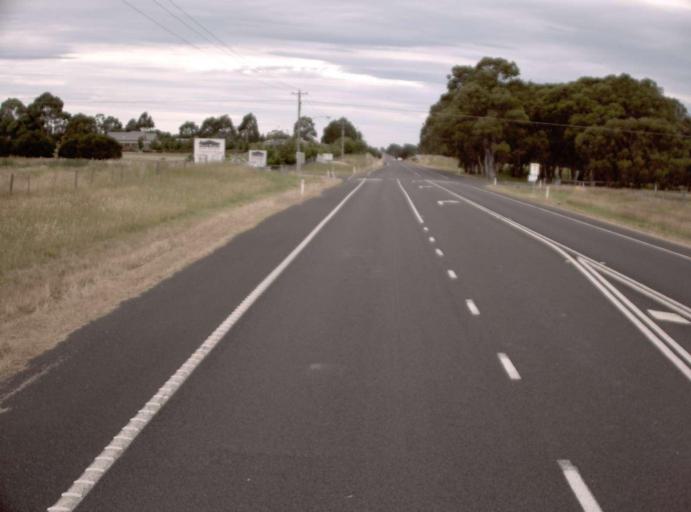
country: AU
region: Victoria
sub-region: East Gippsland
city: Bairnsdale
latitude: -37.8999
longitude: 147.6662
